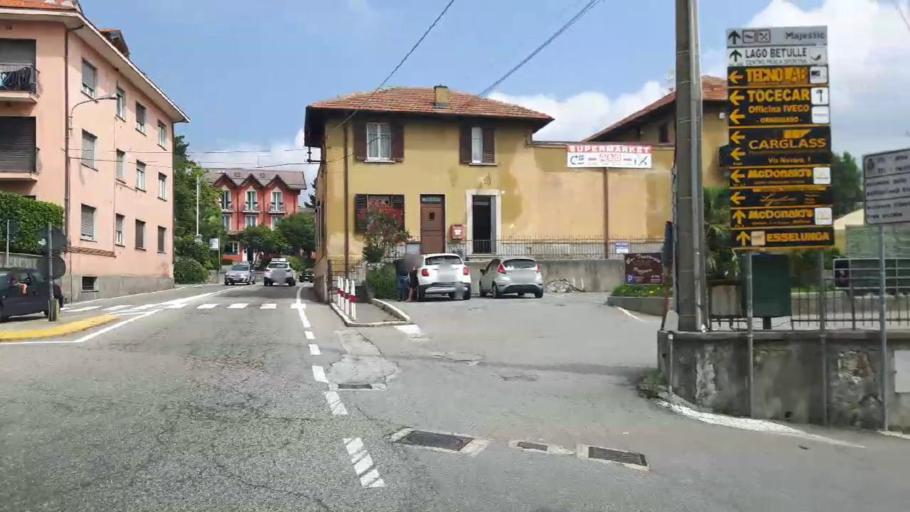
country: IT
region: Piedmont
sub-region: Provincia Verbano-Cusio-Ossola
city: Baveno
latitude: 45.9291
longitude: 8.4795
